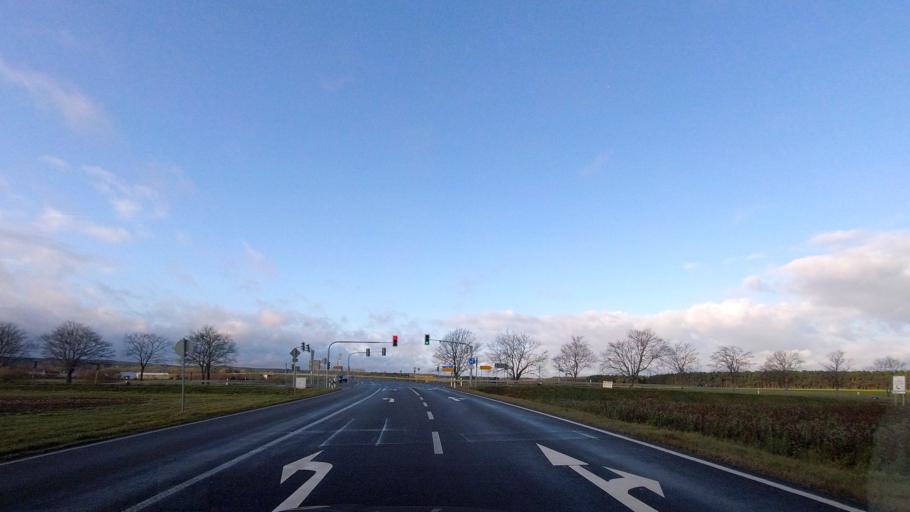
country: DE
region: Brandenburg
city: Belzig
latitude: 52.1460
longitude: 12.6204
